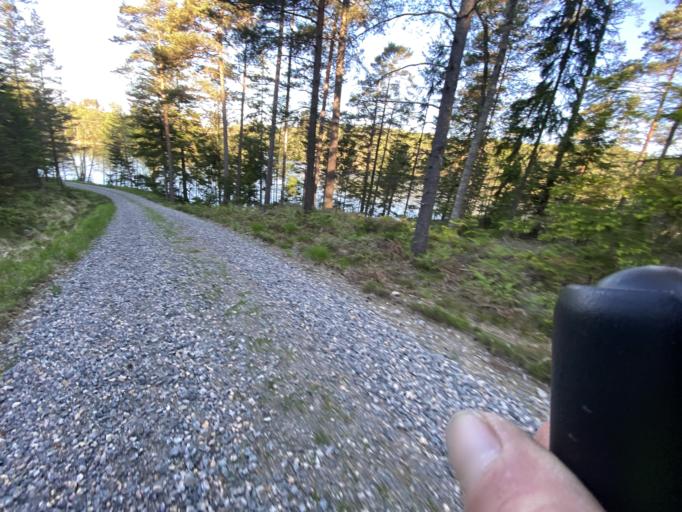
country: SE
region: Vaestra Goetaland
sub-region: Ale Kommun
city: Salanda
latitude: 57.9771
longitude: 12.3771
